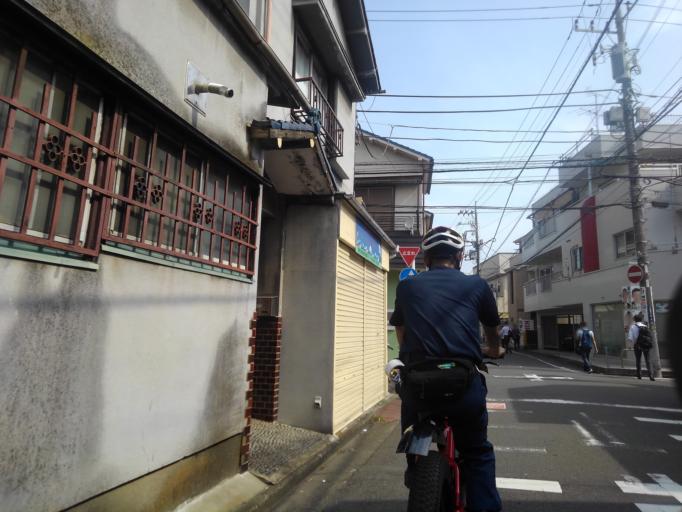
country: JP
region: Kanagawa
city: Minami-rinkan
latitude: 35.4720
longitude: 139.4630
